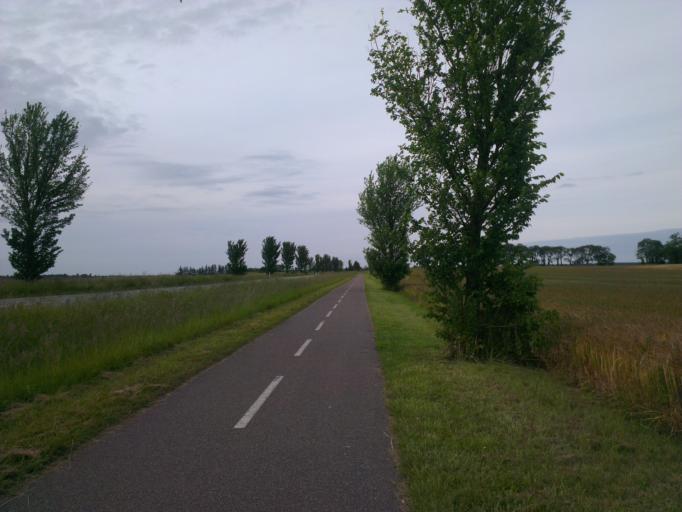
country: DK
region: Capital Region
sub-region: Frederikssund Kommune
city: Jaegerspris
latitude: 55.8163
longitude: 11.9834
